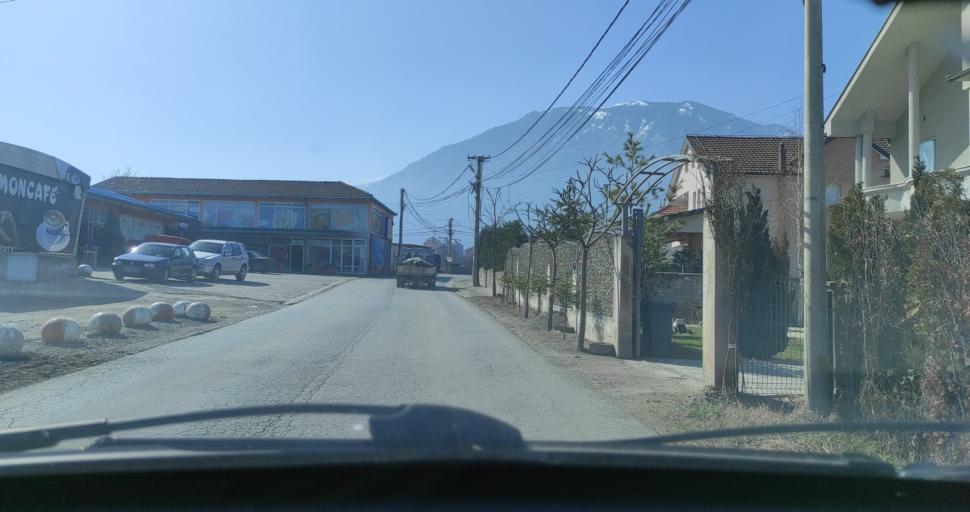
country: XK
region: Pec
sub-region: Komuna e Pejes
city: Peje
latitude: 42.6412
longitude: 20.3021
